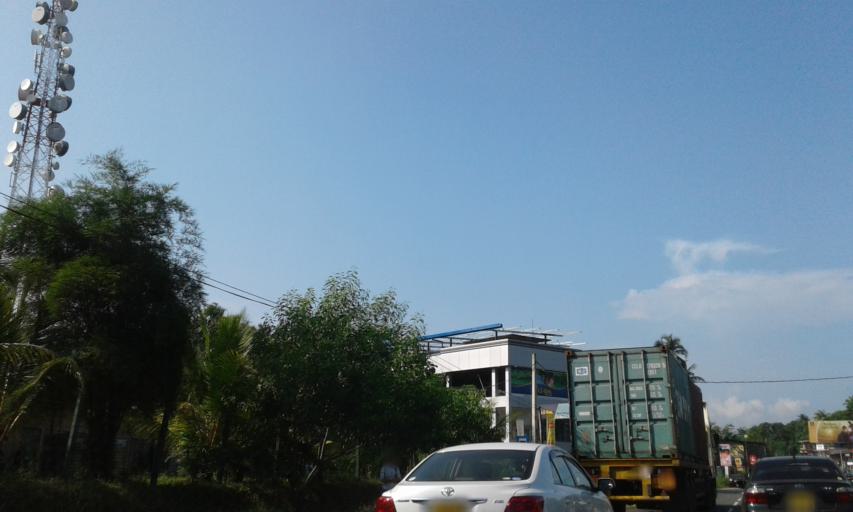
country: LK
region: Western
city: Gampaha
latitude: 7.0207
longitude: 79.9731
